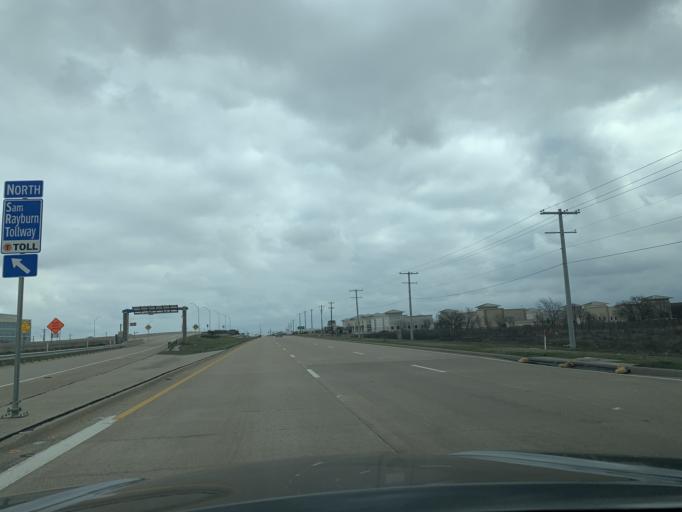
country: US
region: Texas
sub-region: Collin County
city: Allen
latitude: 33.1427
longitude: -96.6831
